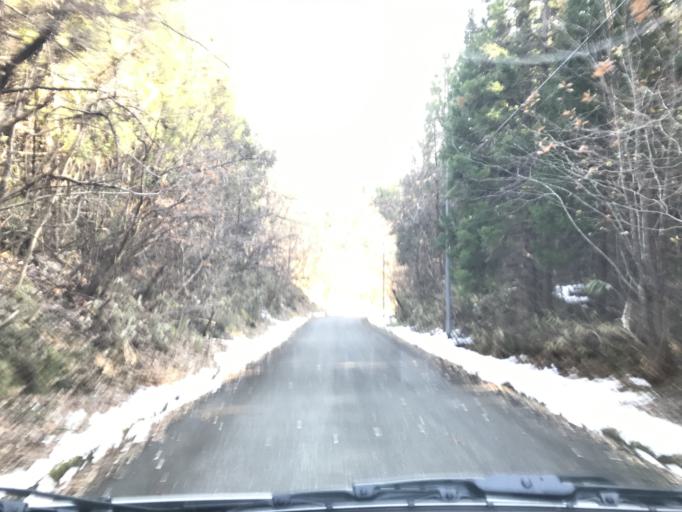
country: JP
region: Iwate
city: Ichinoseki
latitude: 38.9756
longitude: 141.0435
